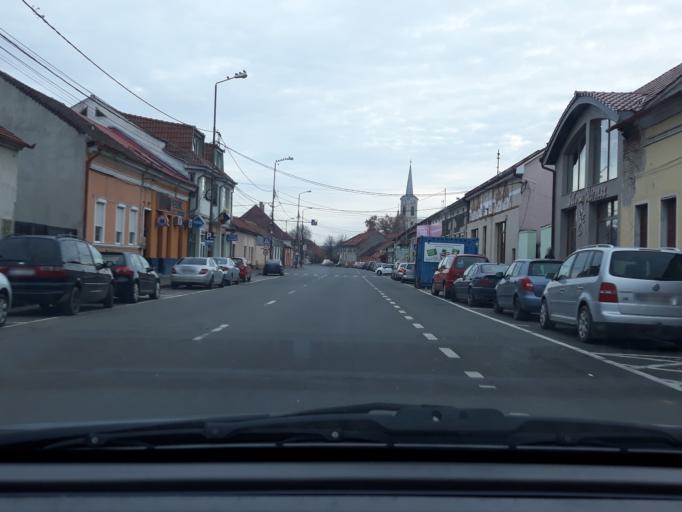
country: RO
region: Bihor
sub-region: Comuna Biharea
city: Oradea
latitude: 47.0516
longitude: 21.9480
